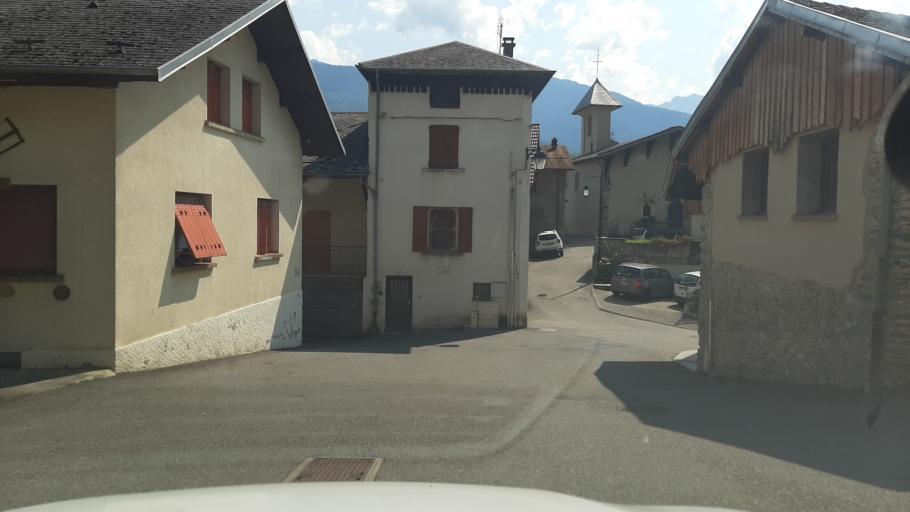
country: FR
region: Rhone-Alpes
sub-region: Departement de la Savoie
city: La Rochette
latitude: 45.4704
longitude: 6.1177
